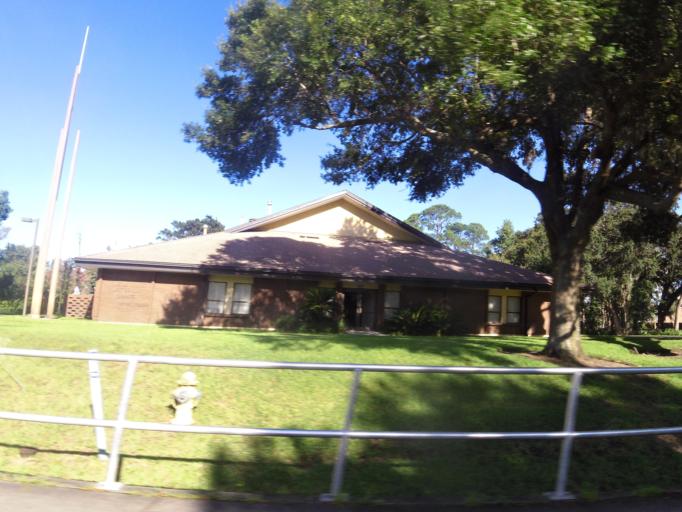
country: US
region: Florida
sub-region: Nassau County
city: Fernandina Beach
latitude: 30.6280
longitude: -81.4551
